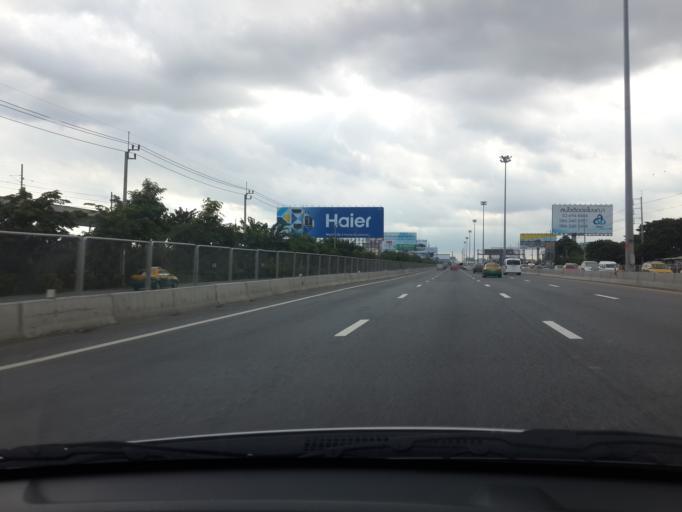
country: TH
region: Bangkok
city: Suan Luang
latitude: 13.7345
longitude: 100.6848
